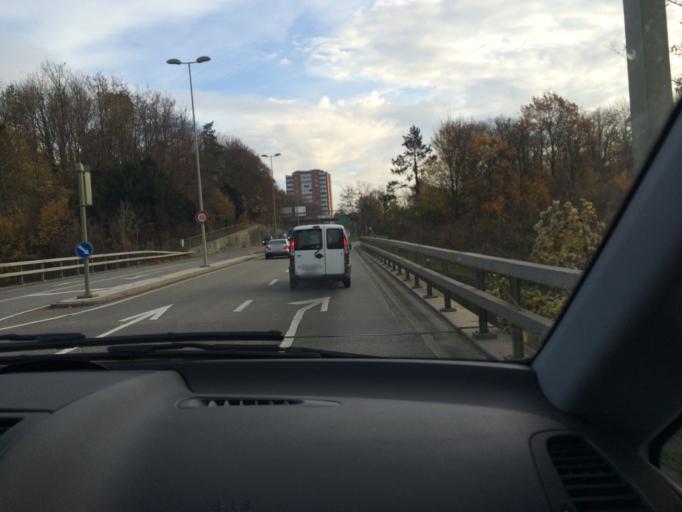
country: CH
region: Basel-Landschaft
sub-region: Bezirk Arlesheim
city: Munchenstein
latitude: 47.5297
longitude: 7.6223
